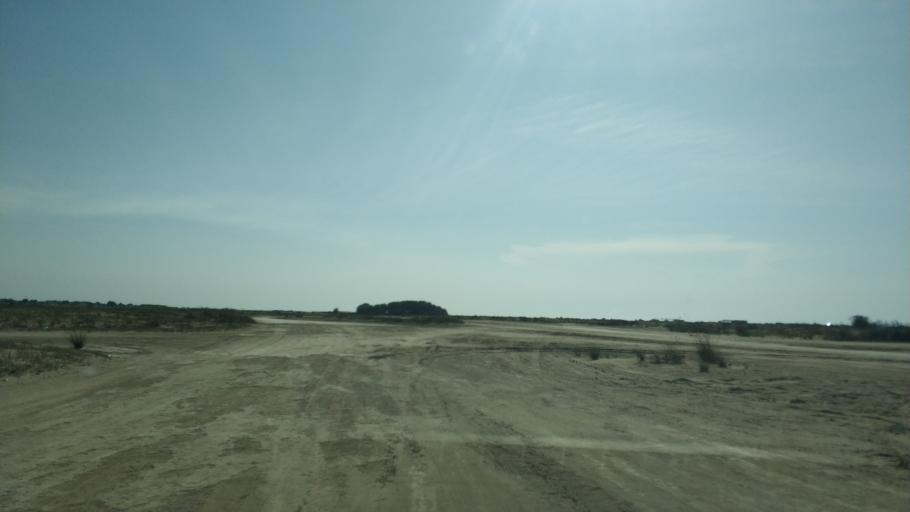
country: AL
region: Fier
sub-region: Rrethi i Lushnjes
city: Divjake
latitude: 40.9610
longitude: 19.4730
